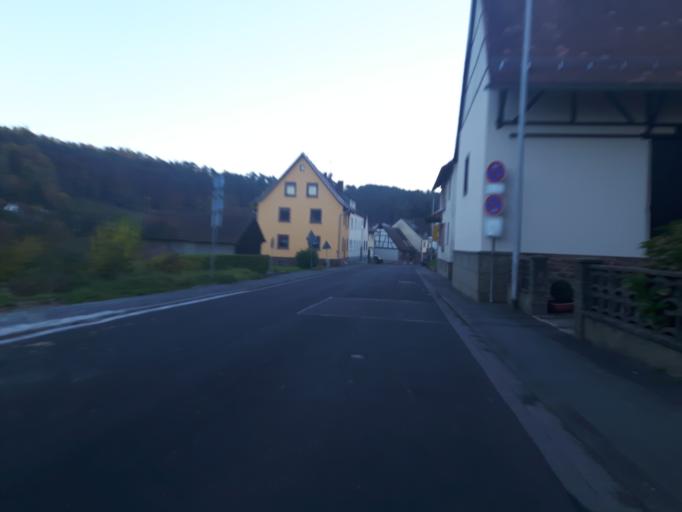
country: DE
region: Bavaria
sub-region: Regierungsbezirk Unterfranken
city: Heimbuchenthal
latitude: 49.8839
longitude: 9.2941
